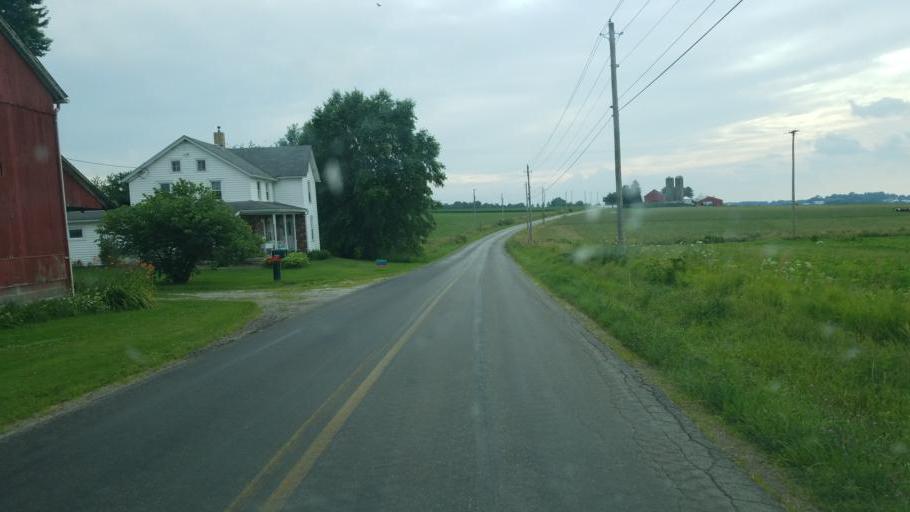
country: US
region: Ohio
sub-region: Wayne County
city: Dalton
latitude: 40.8236
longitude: -81.6677
